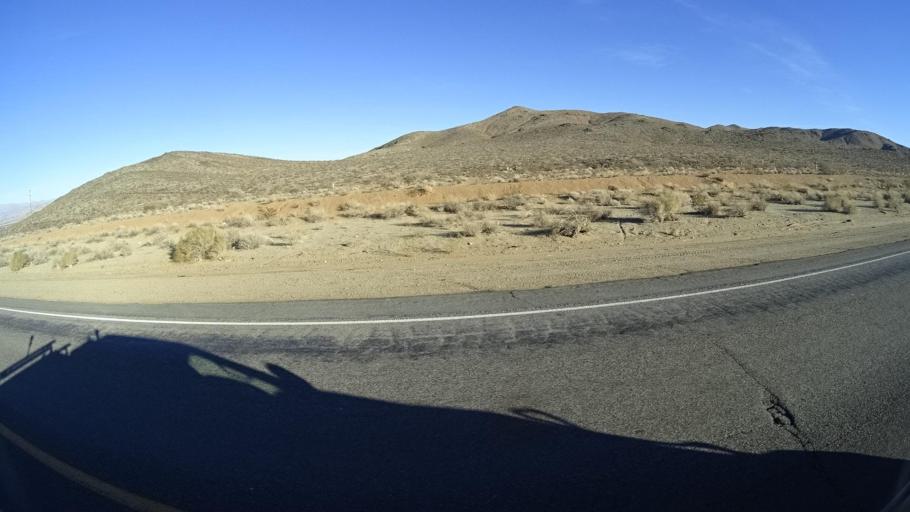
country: US
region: California
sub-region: Kern County
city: Ridgecrest
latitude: 35.5749
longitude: -117.7131
